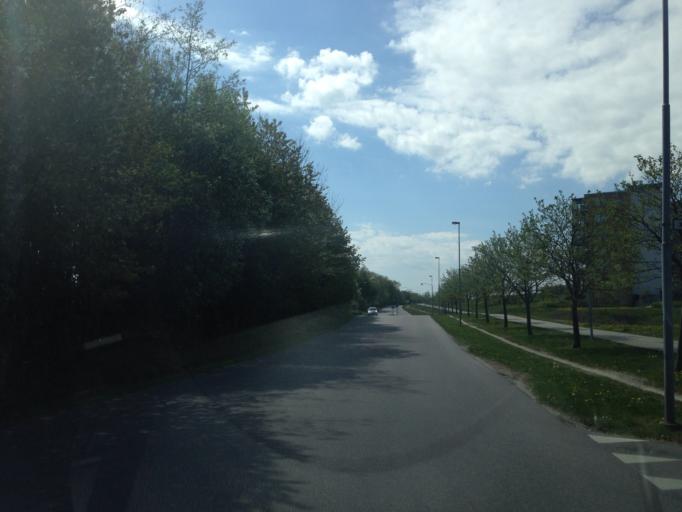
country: SE
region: Skane
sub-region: Lunds Kommun
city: Lund
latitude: 55.7173
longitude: 13.2363
